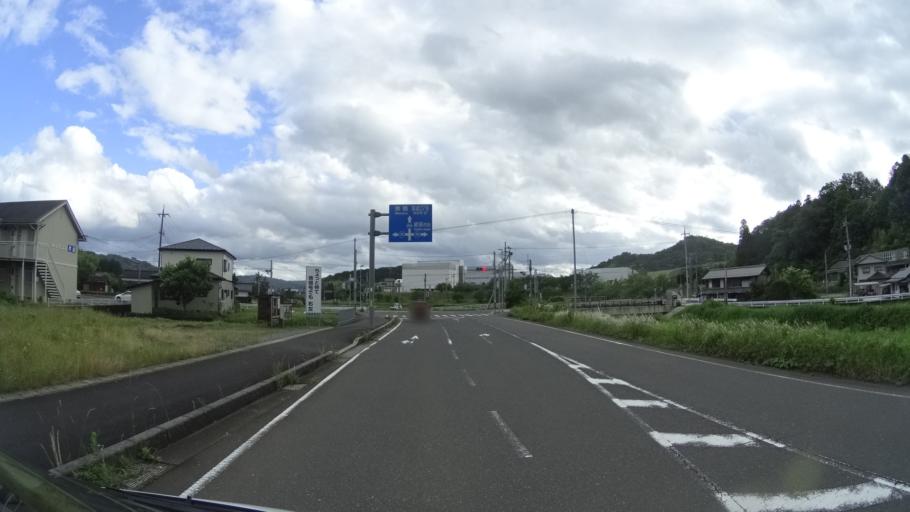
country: JP
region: Kyoto
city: Ayabe
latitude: 35.3347
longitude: 135.2930
